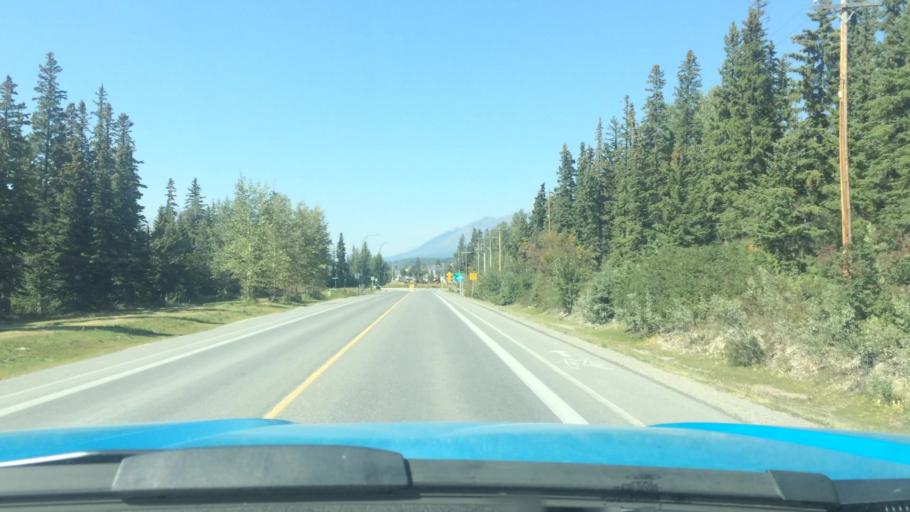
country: CA
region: Alberta
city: Canmore
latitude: 51.0831
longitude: -115.3431
